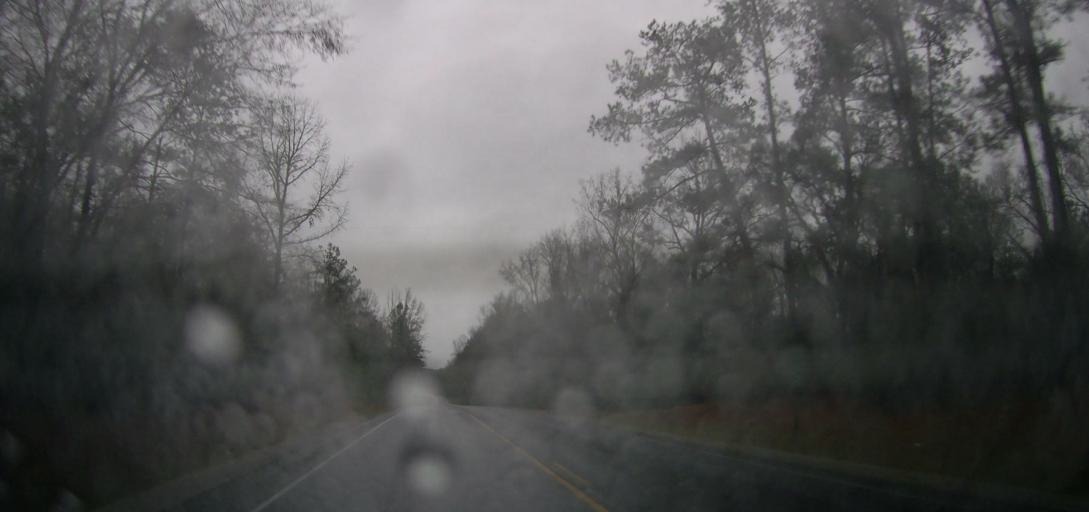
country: US
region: Alabama
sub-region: Autauga County
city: Pine Level
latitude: 32.5615
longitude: -86.6682
